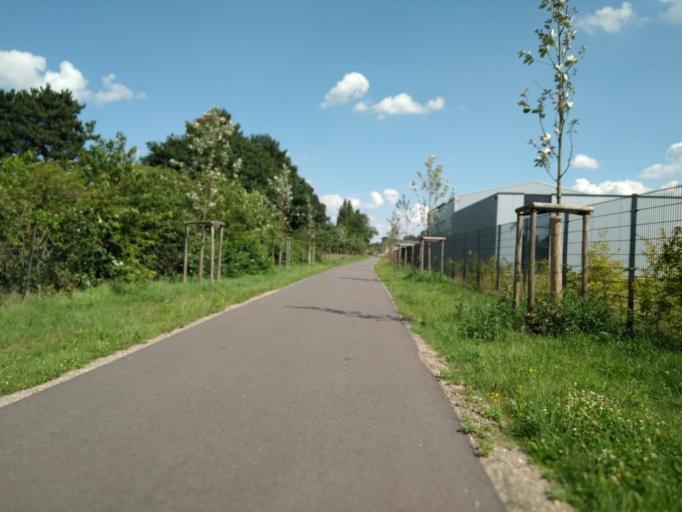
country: DE
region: North Rhine-Westphalia
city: Dorsten
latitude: 51.6729
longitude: 6.9671
